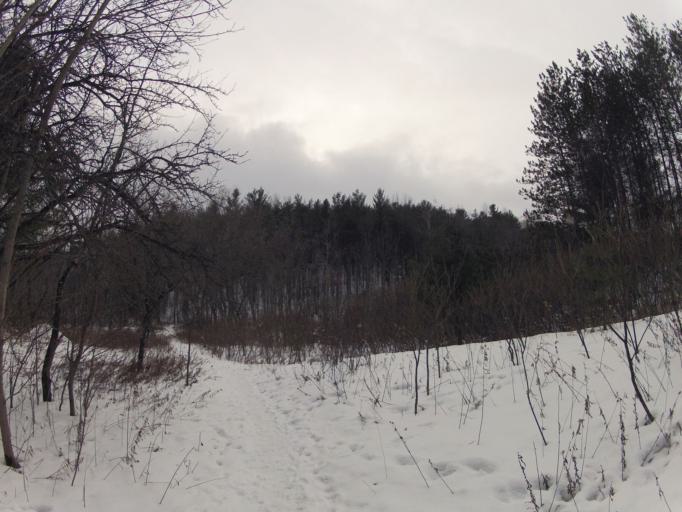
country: CA
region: Ontario
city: Orangeville
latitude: 43.9919
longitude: -80.0500
